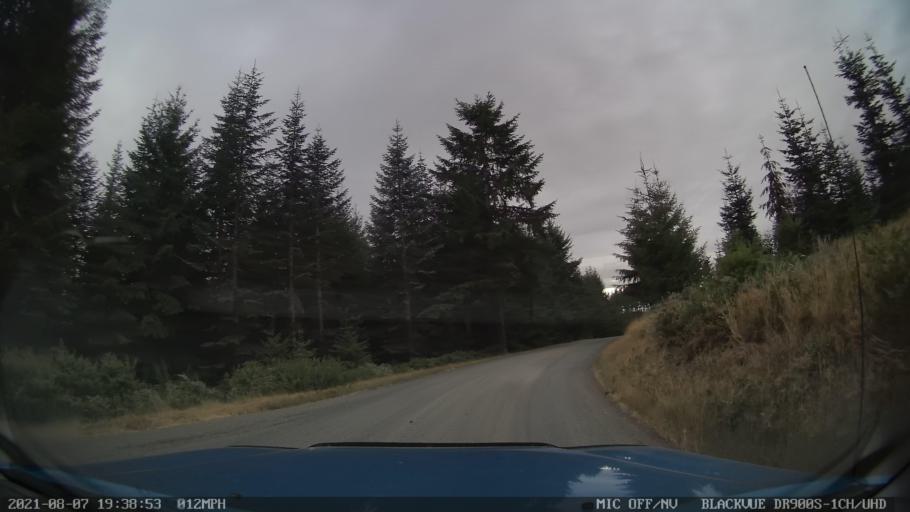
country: US
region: Oregon
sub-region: Marion County
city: Silverton
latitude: 44.9391
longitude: -122.6546
